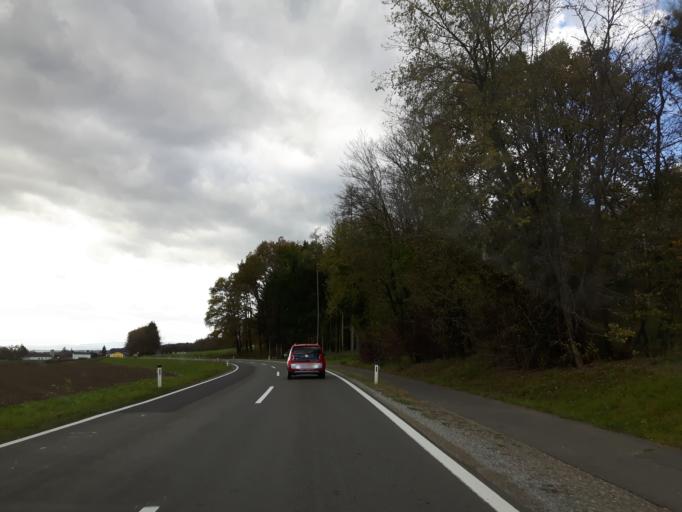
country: AT
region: Styria
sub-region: Politischer Bezirk Suedoststeiermark
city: Kirchbach in Steiermark
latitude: 46.9077
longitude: 15.6695
